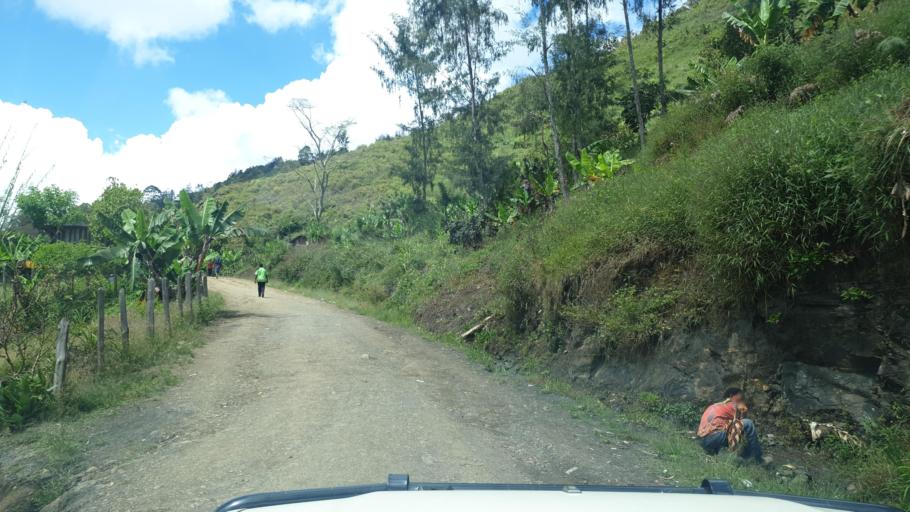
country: PG
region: Eastern Highlands
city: Goroka
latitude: -6.2789
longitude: 145.1840
